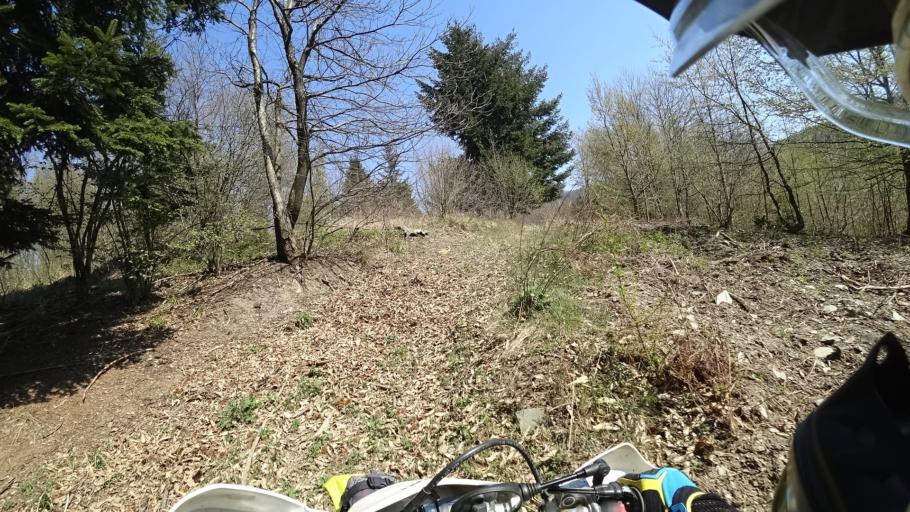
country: HR
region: Zagrebacka
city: Jablanovec
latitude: 45.8938
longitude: 15.9183
